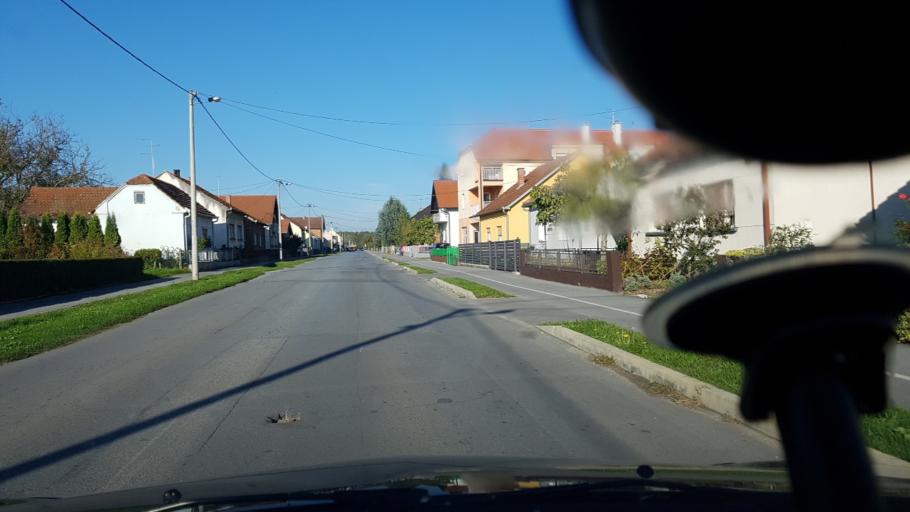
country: HR
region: Bjelovarsko-Bilogorska
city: Bjelovar
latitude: 45.9169
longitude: 16.8584
